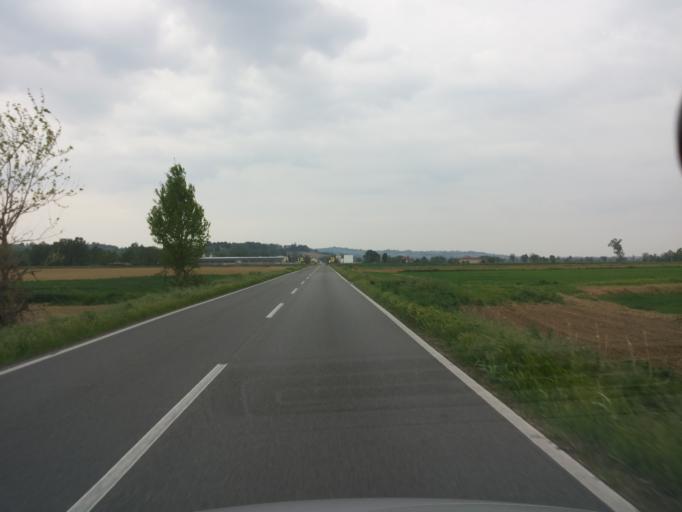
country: IT
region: Piedmont
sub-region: Provincia di Alessandria
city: Terruggia
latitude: 45.0803
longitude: 8.4781
